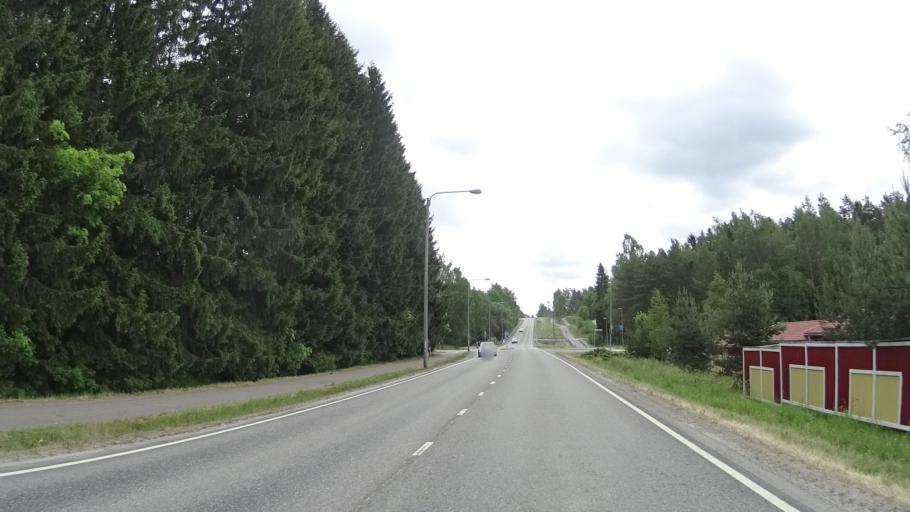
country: FI
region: Uusimaa
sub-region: Helsinki
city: Kirkkonummi
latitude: 60.2721
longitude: 24.4296
